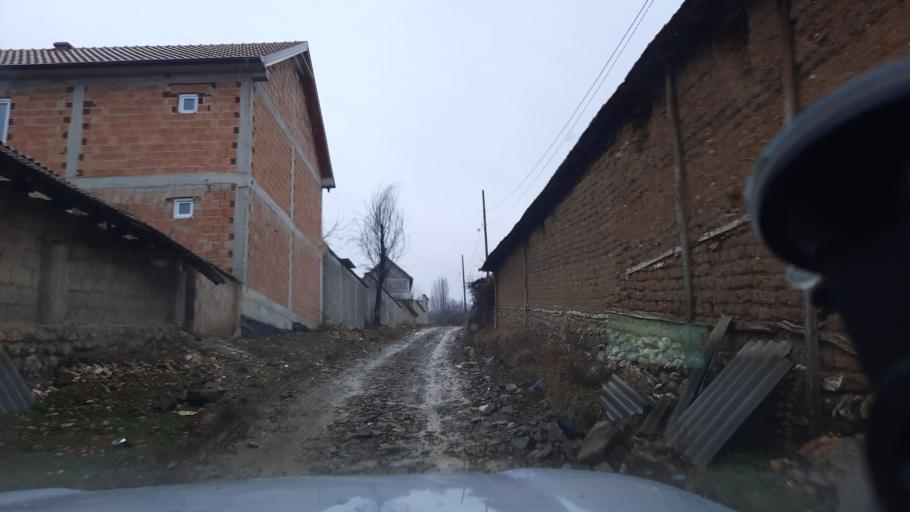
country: MK
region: Opstina Lipkovo
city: Matejche
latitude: 42.1250
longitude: 21.5889
